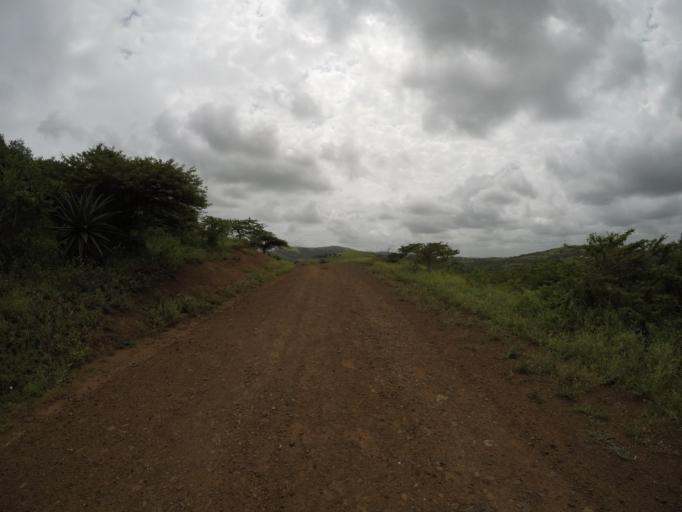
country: ZA
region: KwaZulu-Natal
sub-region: uThungulu District Municipality
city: Empangeni
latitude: -28.6264
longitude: 31.8885
